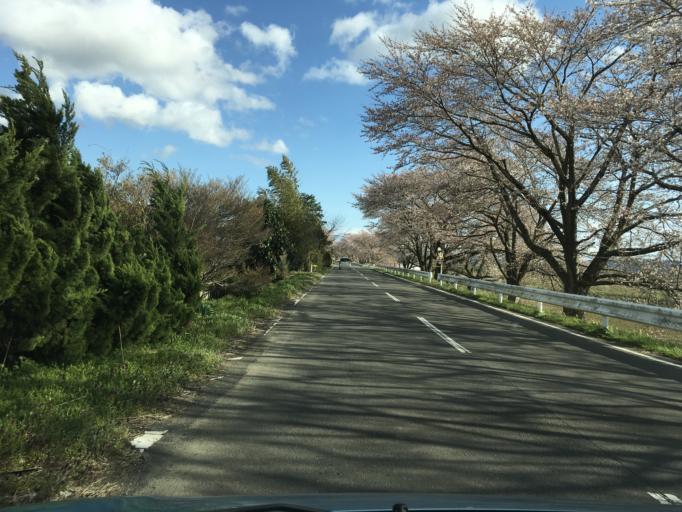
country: JP
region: Miyagi
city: Wakuya
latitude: 38.6487
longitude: 141.1448
